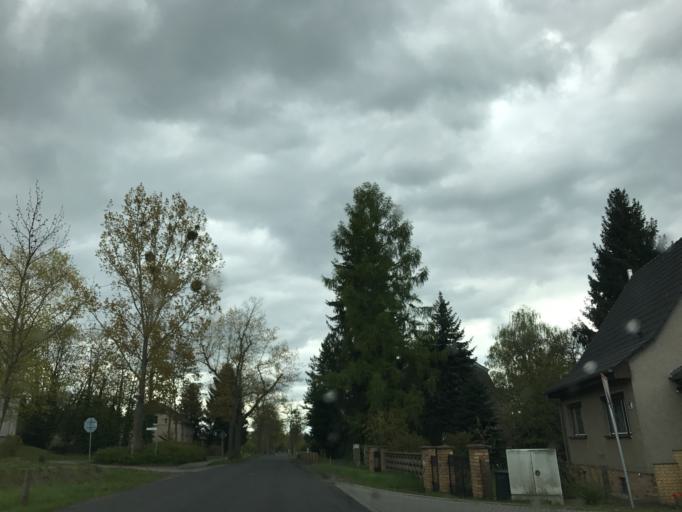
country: DE
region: Brandenburg
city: Wustermark
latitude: 52.4739
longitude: 12.9989
